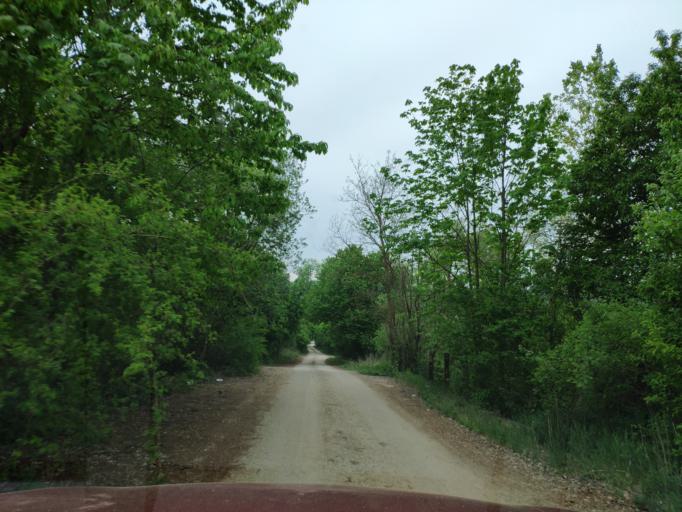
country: SK
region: Kosicky
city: Roznava
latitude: 48.5739
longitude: 20.6517
